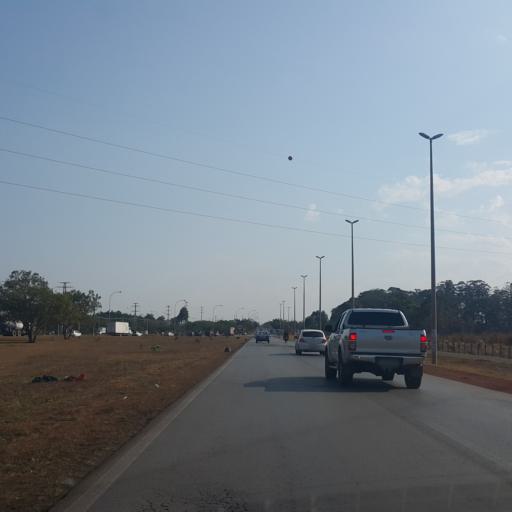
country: BR
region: Federal District
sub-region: Brasilia
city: Brasilia
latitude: -15.8725
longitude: -48.0435
